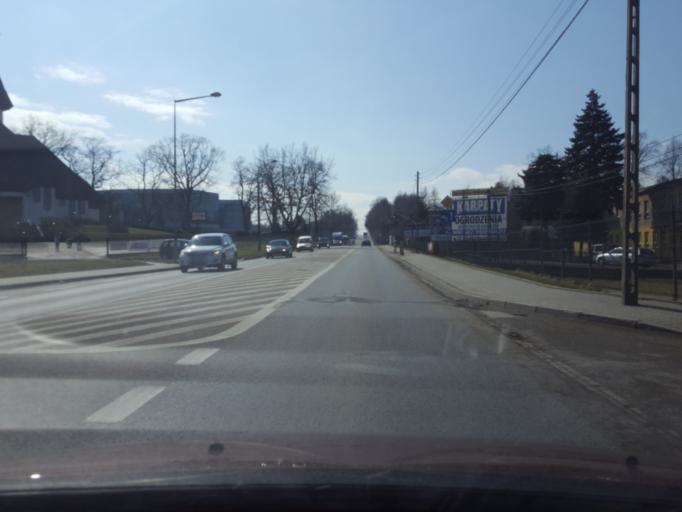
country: PL
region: Lesser Poland Voivodeship
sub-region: Powiat nowosadecki
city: Nowy Sacz
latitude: 49.6491
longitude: 20.6904
